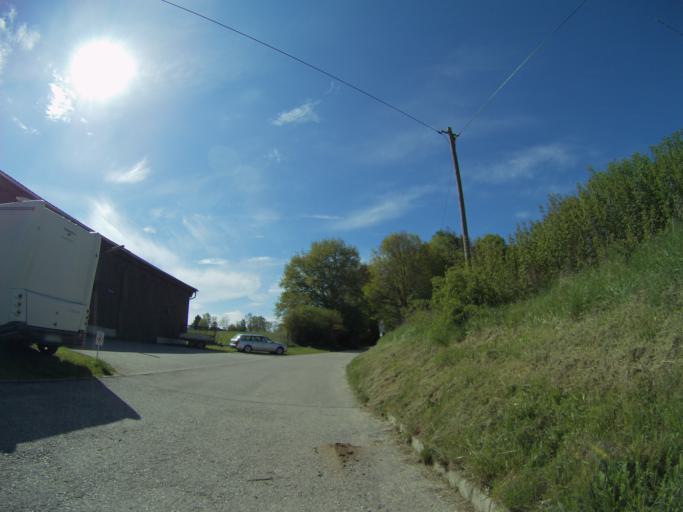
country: DE
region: Bavaria
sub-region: Upper Bavaria
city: Freising
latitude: 48.4092
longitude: 11.7670
